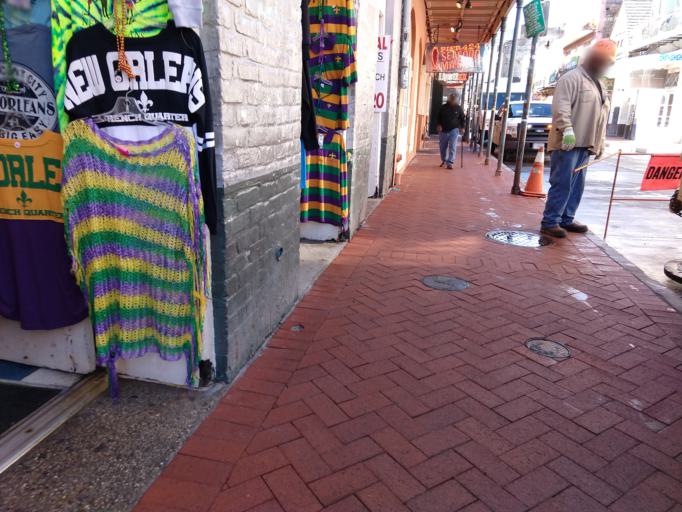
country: US
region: Louisiana
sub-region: Orleans Parish
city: New Orleans
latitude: 29.9570
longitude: -90.0672
